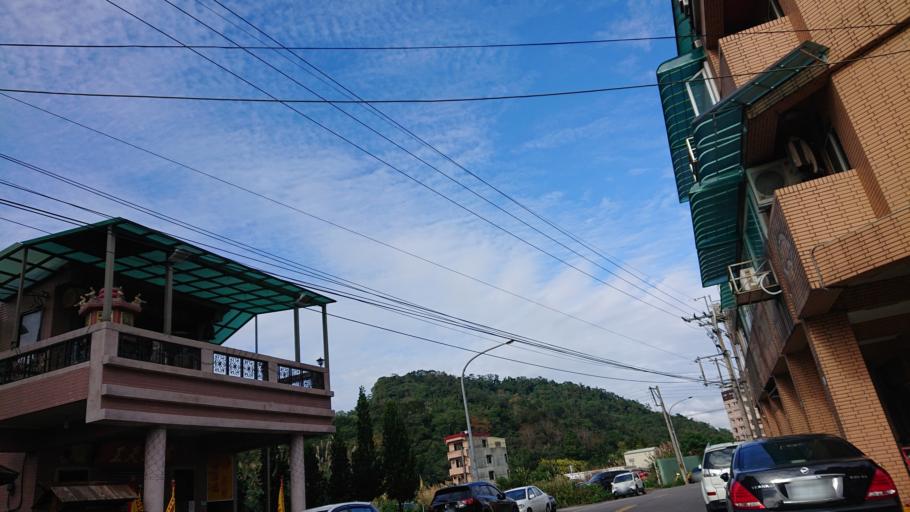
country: TW
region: Taiwan
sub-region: Taoyuan
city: Taoyuan
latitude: 24.9245
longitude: 121.3632
